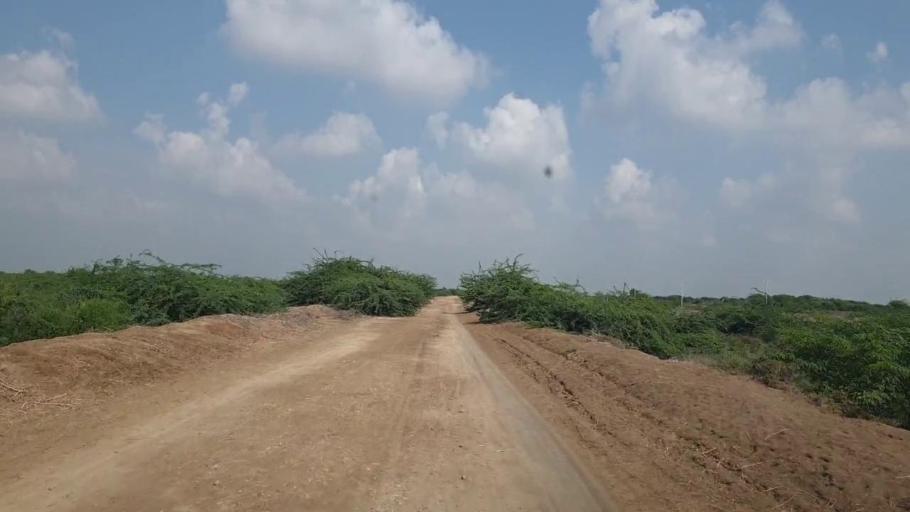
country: PK
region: Sindh
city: Badin
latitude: 24.4864
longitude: 68.6493
